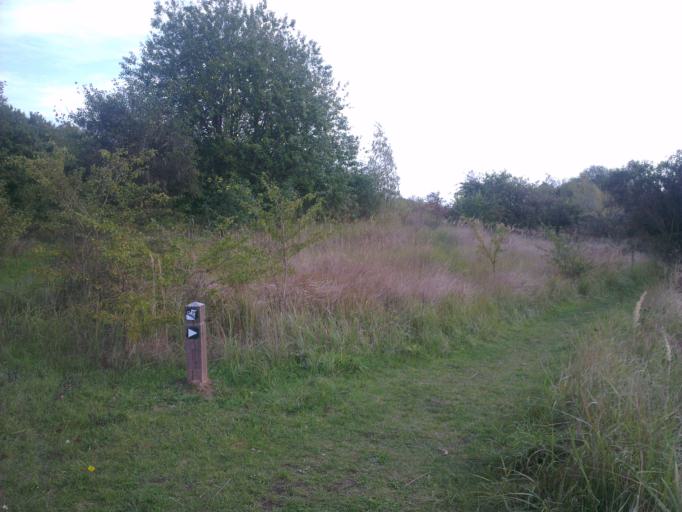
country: DK
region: Capital Region
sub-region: Frederikssund Kommune
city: Frederikssund
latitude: 55.8346
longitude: 12.0919
